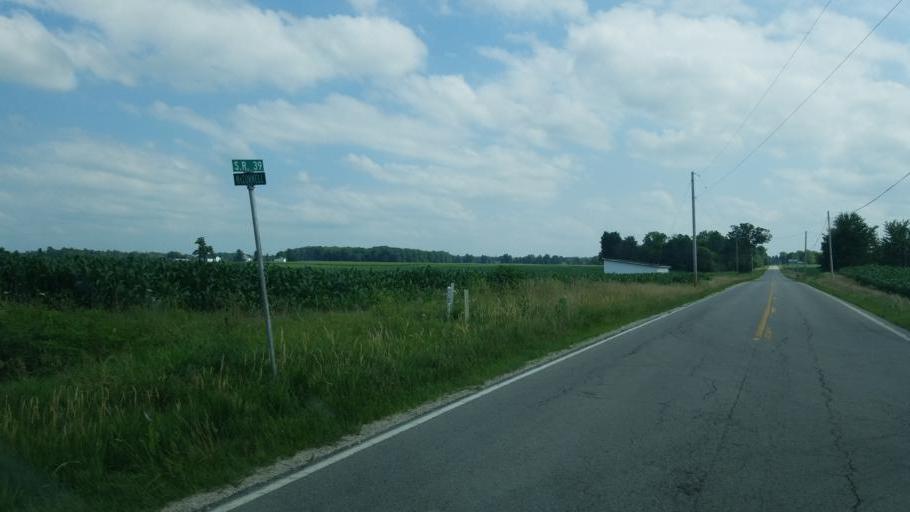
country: US
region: Ohio
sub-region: Richland County
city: Shelby
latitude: 40.9239
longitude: -82.7723
